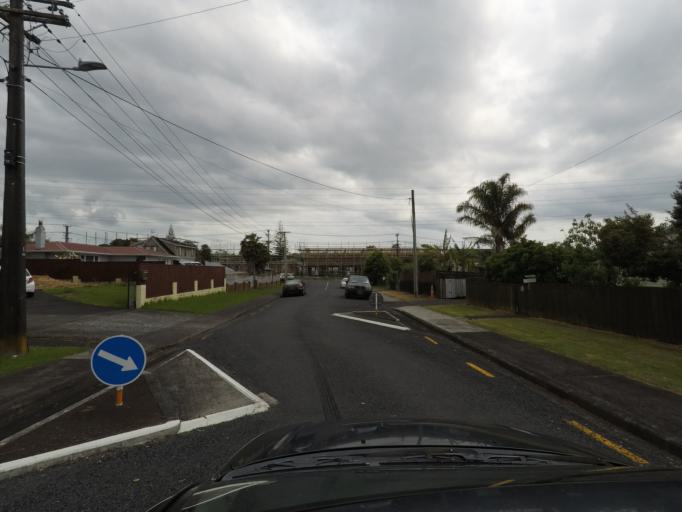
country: NZ
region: Auckland
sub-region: Auckland
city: Rosebank
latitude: -36.8551
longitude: 174.6498
